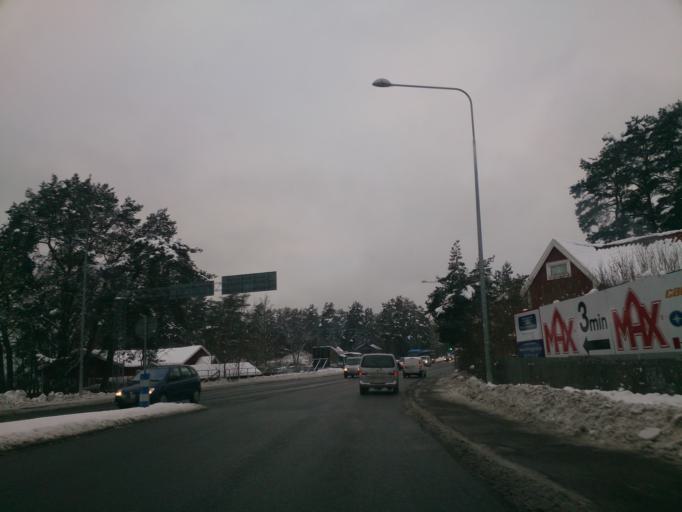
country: SE
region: Stockholm
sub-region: Varmdo Kommun
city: Mortnas
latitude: 59.3132
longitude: 18.4582
